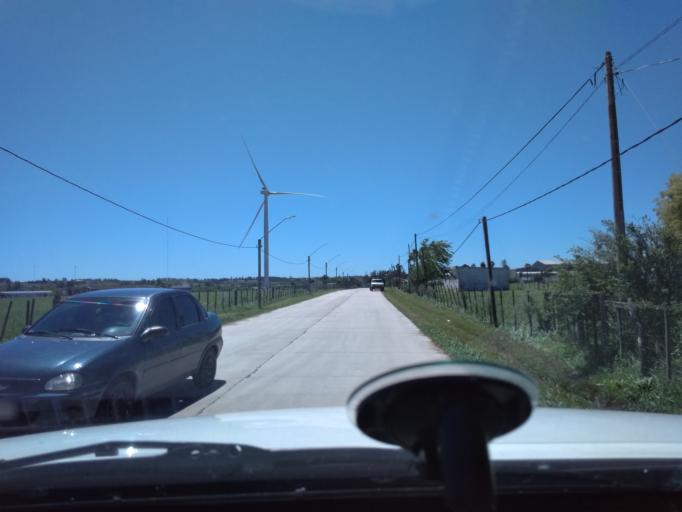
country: UY
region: Canelones
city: Progreso
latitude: -34.6908
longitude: -56.2984
